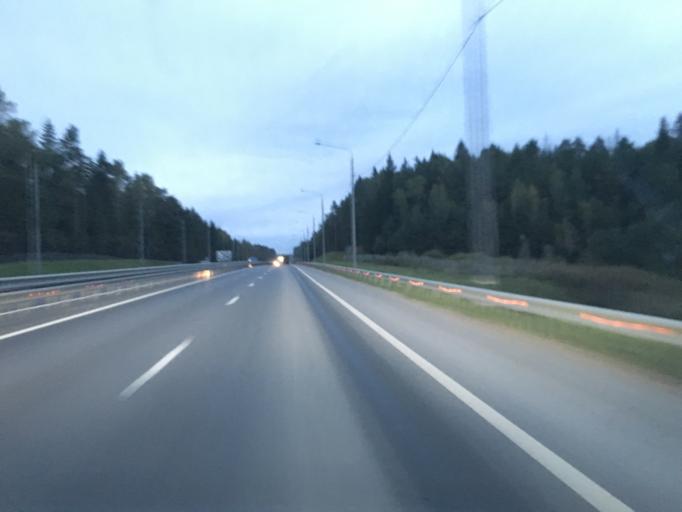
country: RU
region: Kaluga
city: Maloyaroslavets
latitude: 54.9296
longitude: 36.4128
